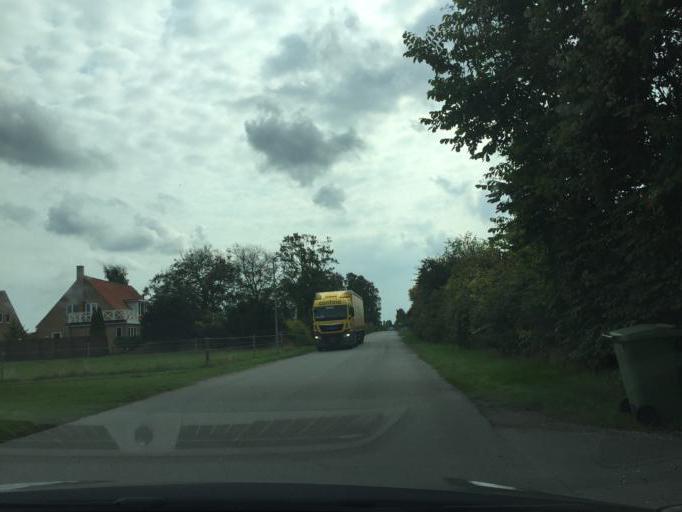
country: DK
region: South Denmark
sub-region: Odense Kommune
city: Stige
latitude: 55.4456
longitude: 10.4019
